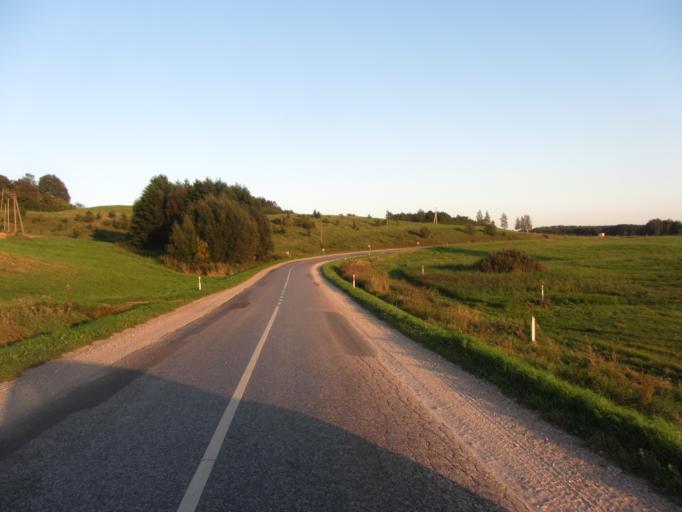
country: LT
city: Lazdijai
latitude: 54.3149
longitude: 23.5430
